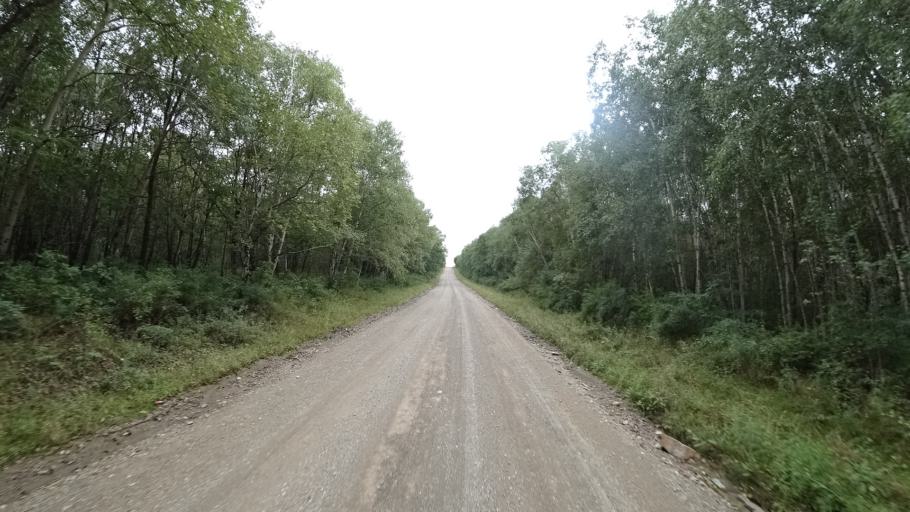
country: RU
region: Primorskiy
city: Ivanovka
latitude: 44.0391
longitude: 132.4969
